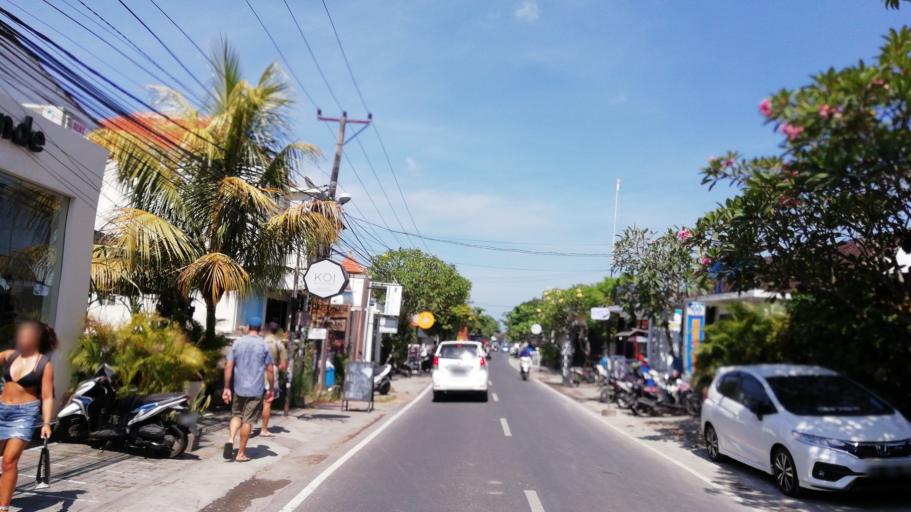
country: ID
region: Bali
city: Banjar Kerobokan
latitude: -8.6497
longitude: 115.1372
